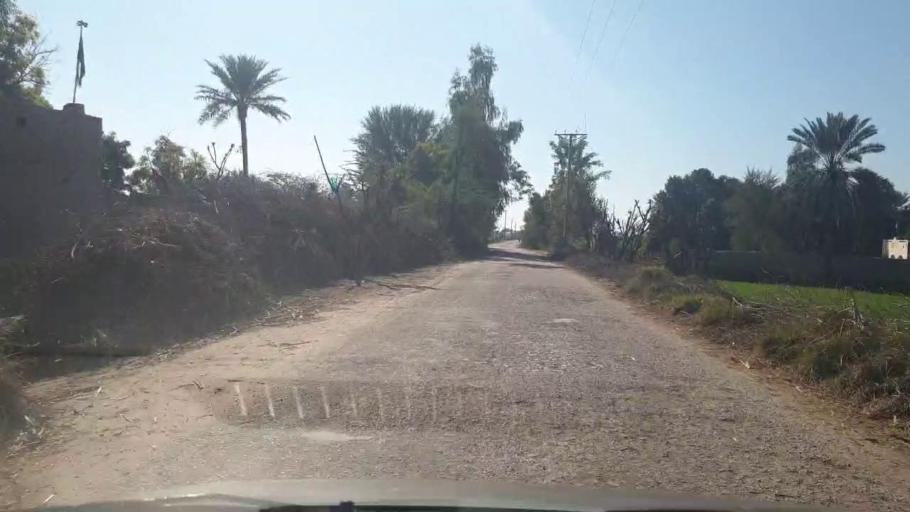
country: PK
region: Sindh
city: Bozdar
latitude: 27.2594
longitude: 68.6527
